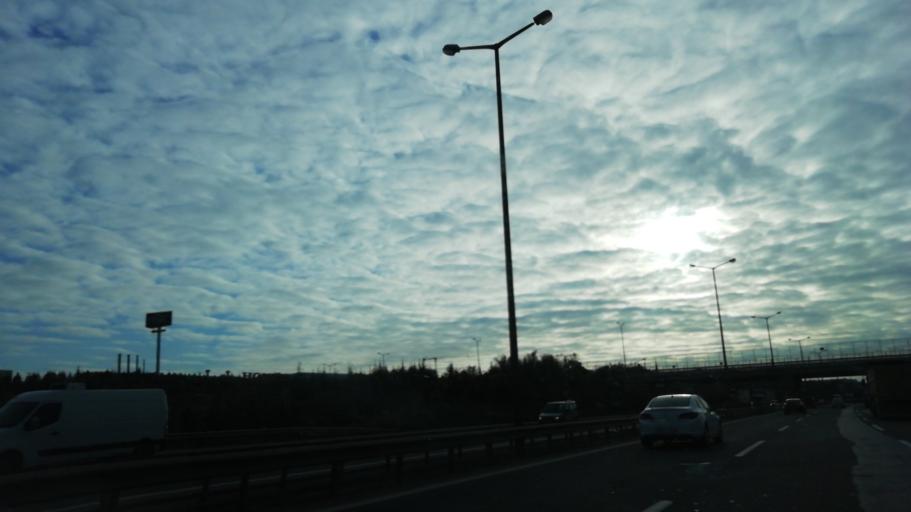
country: TR
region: Kocaeli
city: Balcik
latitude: 40.8716
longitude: 29.3946
